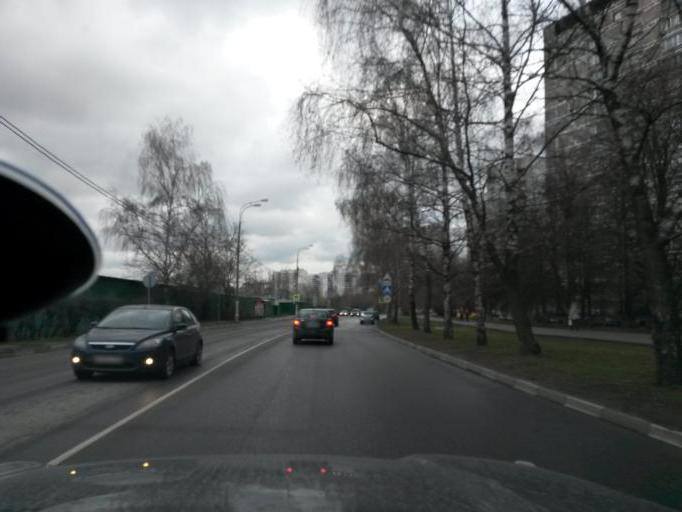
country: RU
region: Moscow
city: Orekhovo-Borisovo
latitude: 55.6237
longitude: 37.7312
